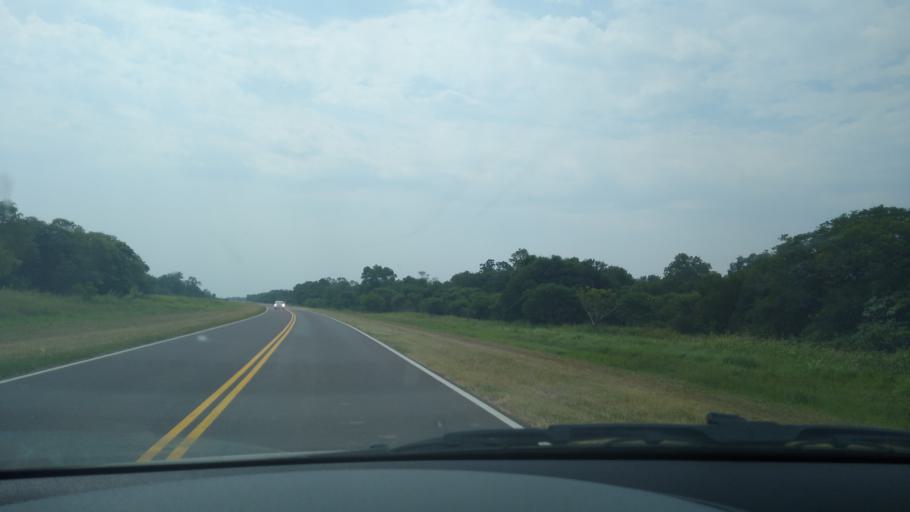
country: AR
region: Chaco
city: Margarita Belen
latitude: -27.0483
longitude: -58.9623
